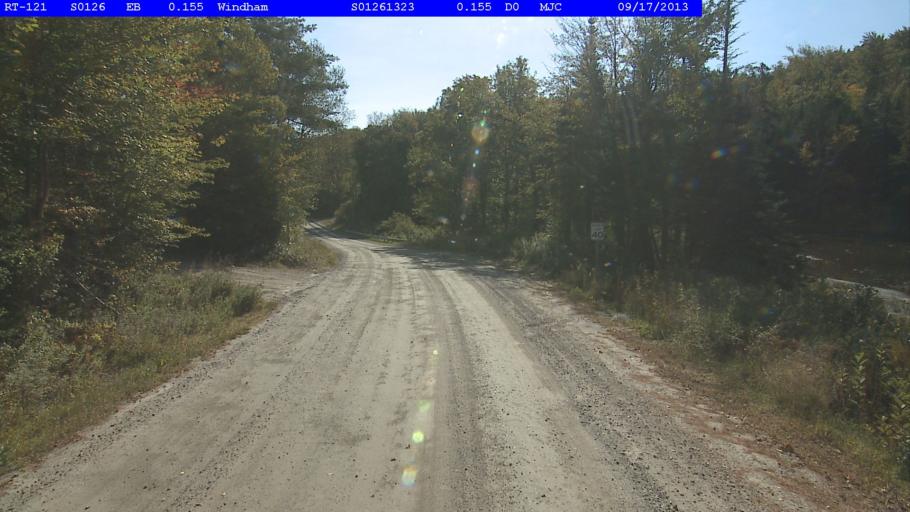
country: US
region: Vermont
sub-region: Windsor County
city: Chester
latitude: 43.1963
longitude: -72.7171
